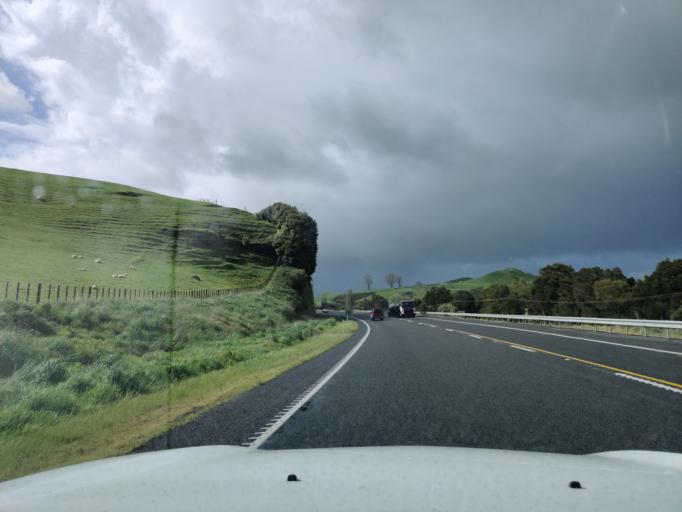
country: NZ
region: Waikato
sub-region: Matamata-Piako District
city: Matamata
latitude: -37.9507
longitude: 175.6748
